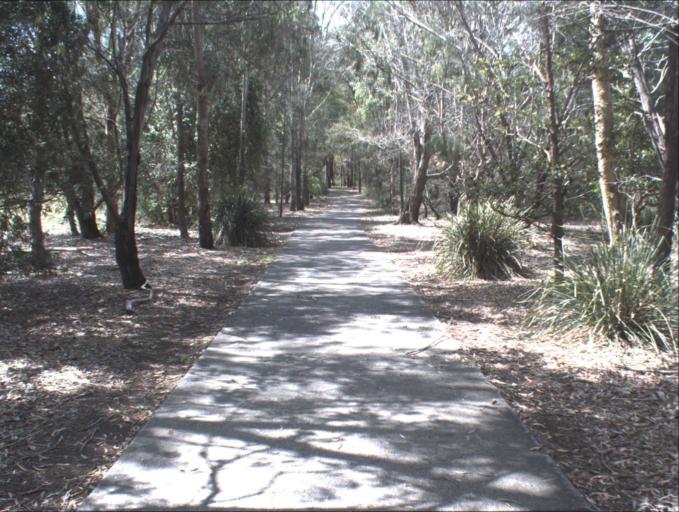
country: AU
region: Queensland
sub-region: Logan
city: Slacks Creek
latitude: -27.6722
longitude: 153.1553
